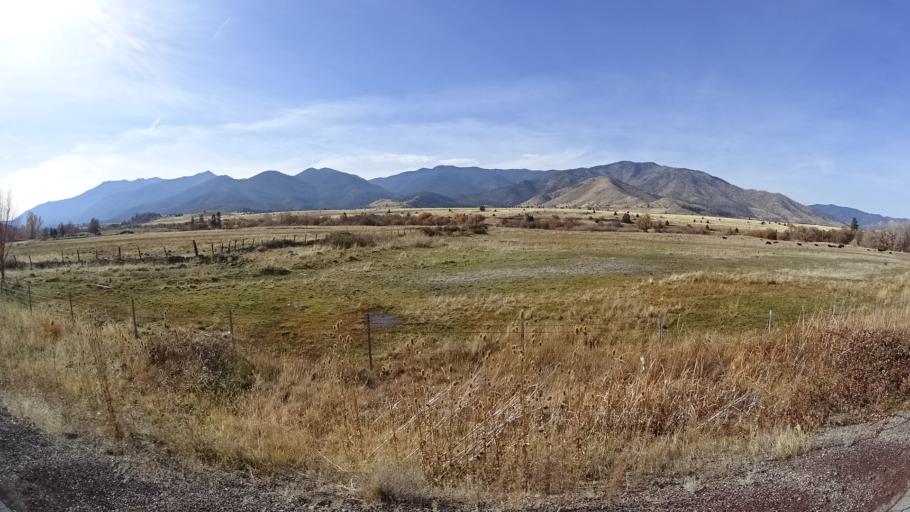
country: US
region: California
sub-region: Siskiyou County
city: Weed
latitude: 41.4695
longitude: -122.4352
